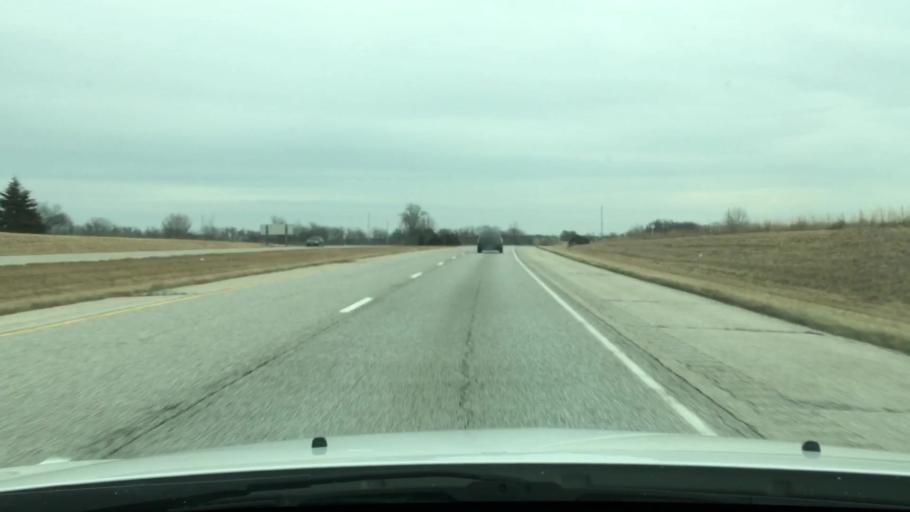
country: US
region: Illinois
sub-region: Pike County
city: Griggsville
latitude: 39.6775
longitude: -90.7281
